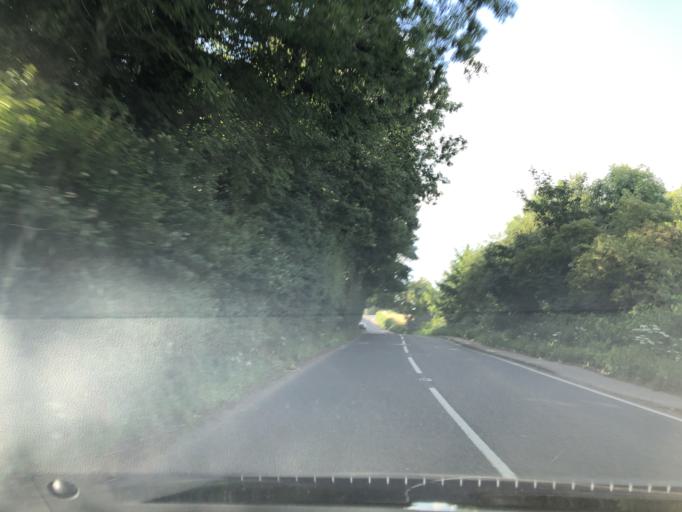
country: GB
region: Northern Ireland
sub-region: Ards District
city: Comber
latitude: 54.5601
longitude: -5.7615
